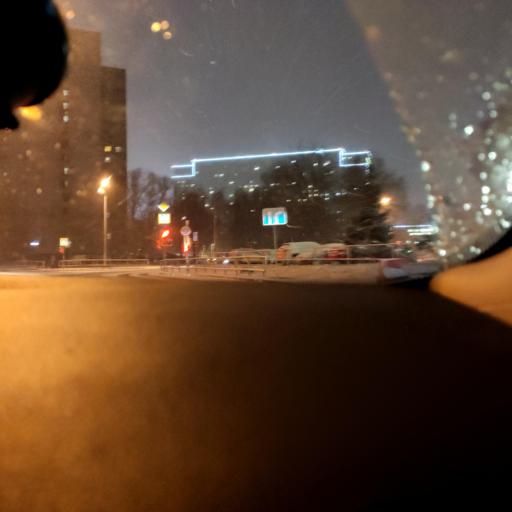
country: RU
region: Moscow
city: Babushkin
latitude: 55.8757
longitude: 37.7268
